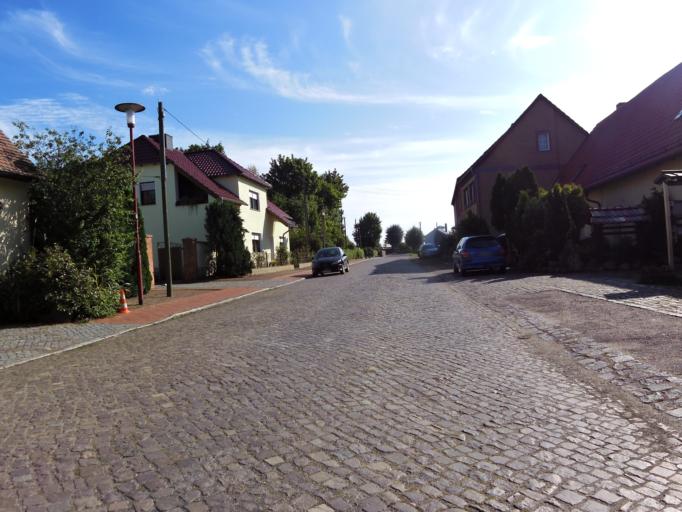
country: DE
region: Saxony-Anhalt
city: Nudersdorf
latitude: 51.8722
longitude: 12.5403
